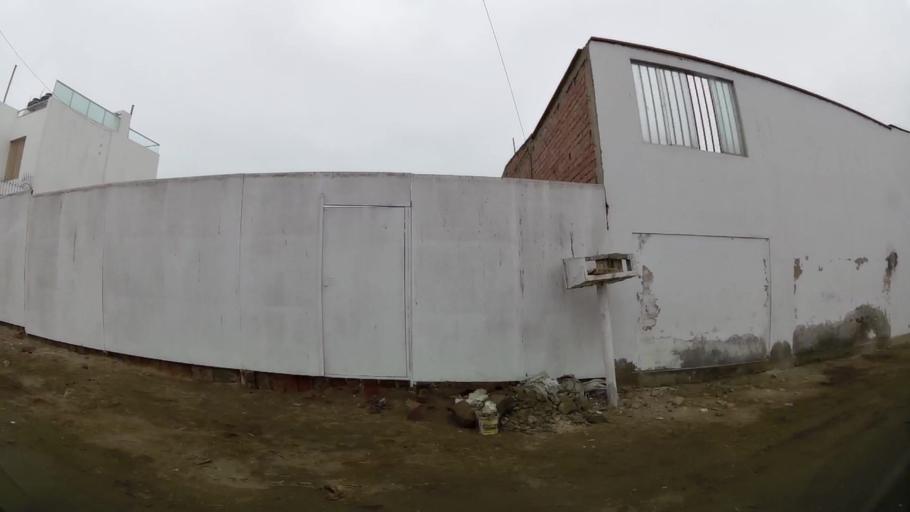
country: PE
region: Lima
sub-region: Lima
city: Punta Hermosa
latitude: -12.3362
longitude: -76.8267
